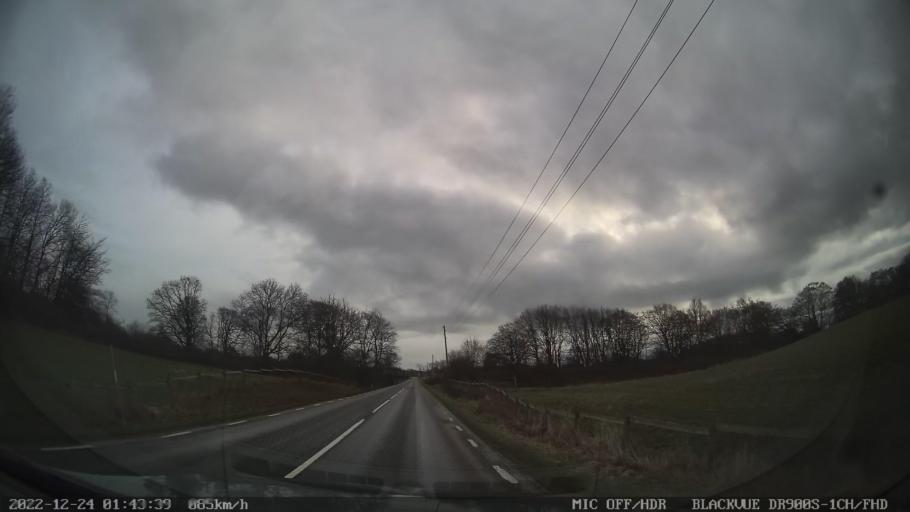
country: SE
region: Skane
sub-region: Tomelilla Kommun
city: Tomelilla
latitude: 55.5971
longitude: 14.0864
